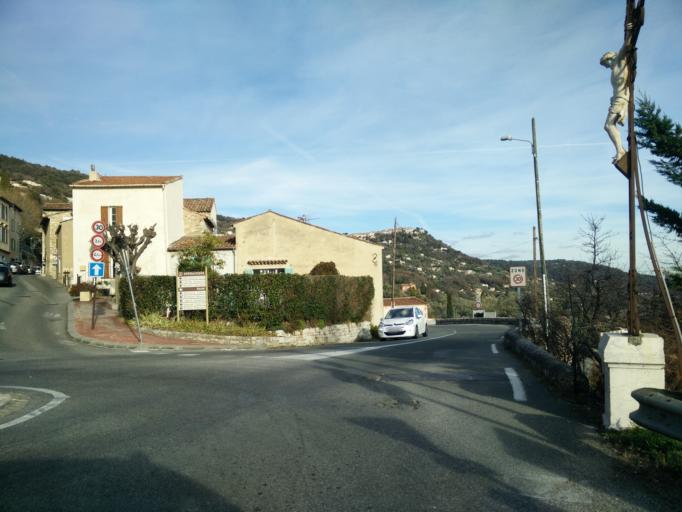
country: FR
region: Provence-Alpes-Cote d'Azur
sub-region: Departement des Alpes-Maritimes
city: Speracedes
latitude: 43.6474
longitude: 6.8579
